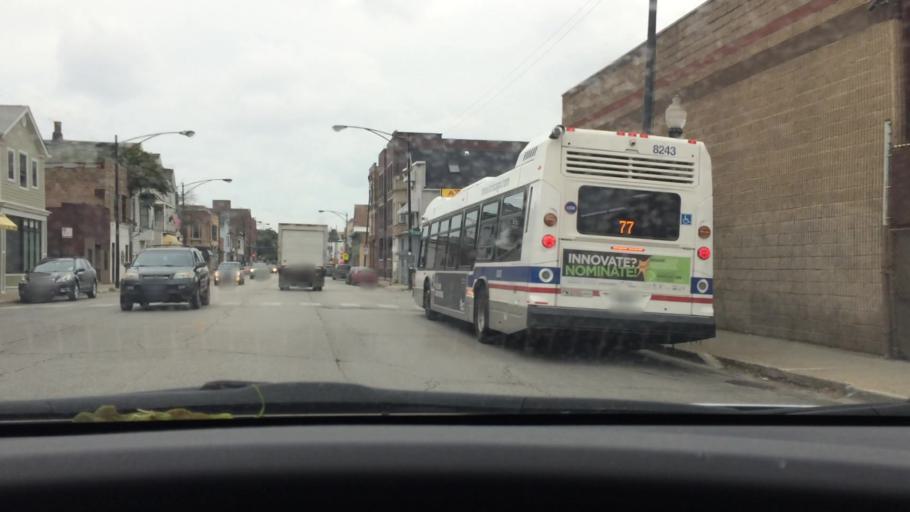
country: US
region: Illinois
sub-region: Cook County
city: Lincolnwood
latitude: 41.9393
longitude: -87.7052
